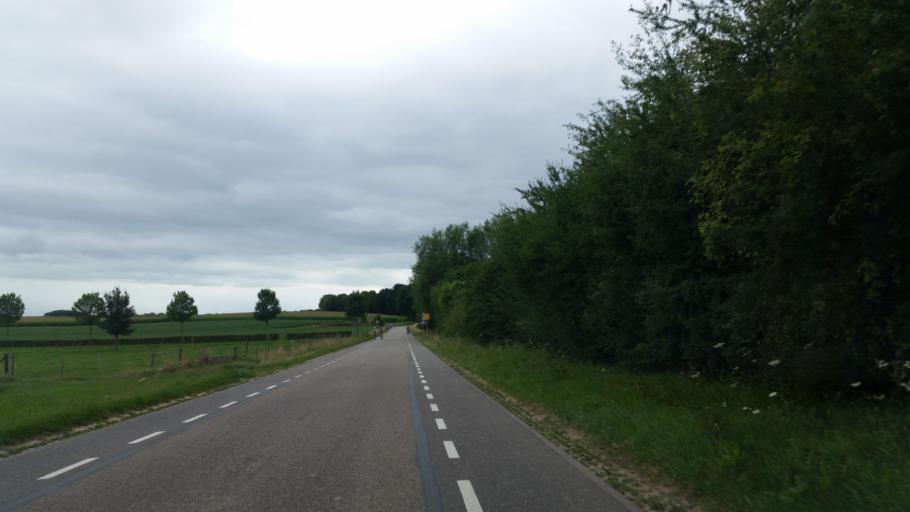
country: NL
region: Limburg
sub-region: Valkenburg aan de Geul
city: Sibbe
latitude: 50.8390
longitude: 5.8213
